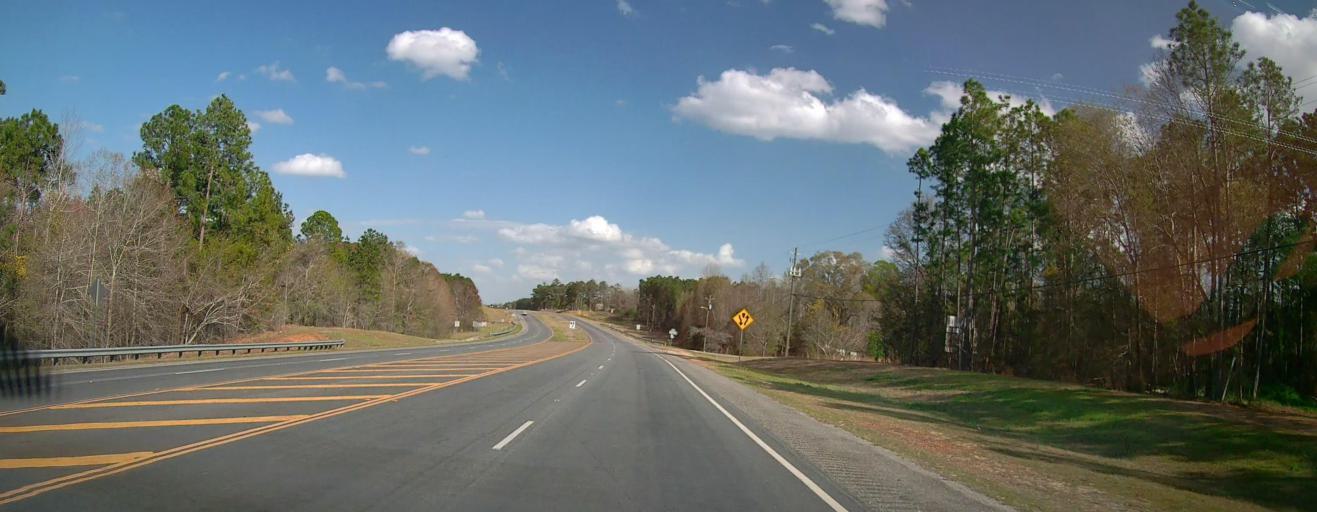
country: US
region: Georgia
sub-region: Telfair County
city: Helena
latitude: 32.1021
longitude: -83.0552
